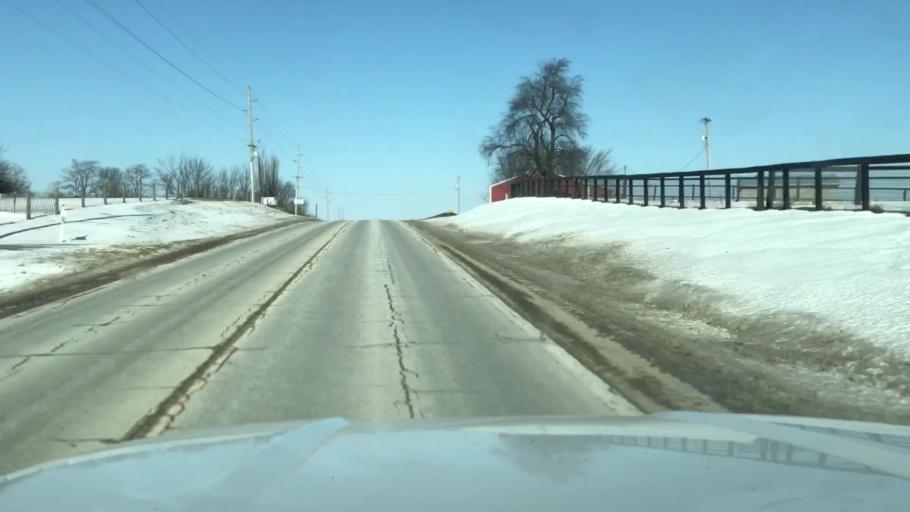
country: US
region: Missouri
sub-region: Andrew County
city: Savannah
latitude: 39.9534
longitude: -94.8478
